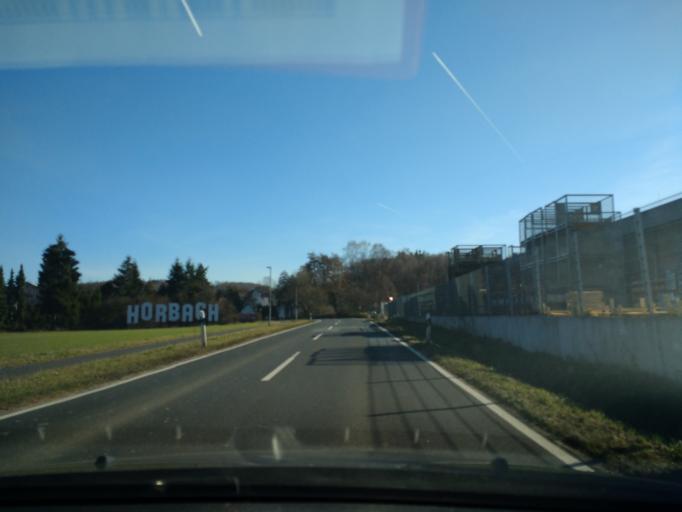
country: DE
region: Bavaria
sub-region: Regierungsbezirk Unterfranken
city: Geiselbach
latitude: 50.1378
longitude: 9.1537
